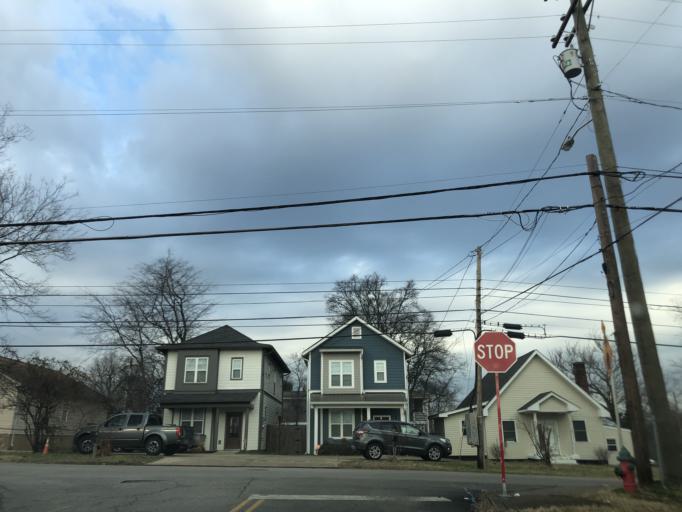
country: US
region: Tennessee
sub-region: Davidson County
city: Nashville
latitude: 36.2019
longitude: -86.7361
